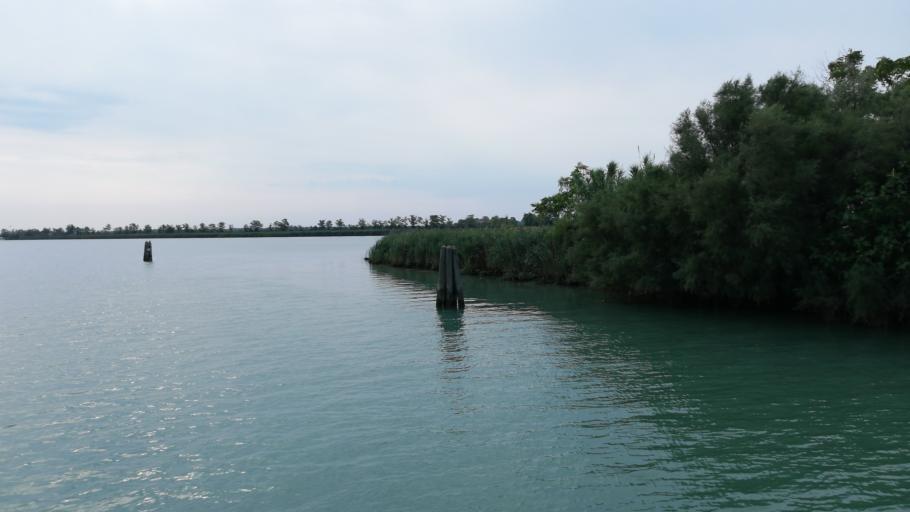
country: IT
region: Veneto
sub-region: Provincia di Venezia
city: Caorle
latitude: 45.6294
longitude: 12.8937
